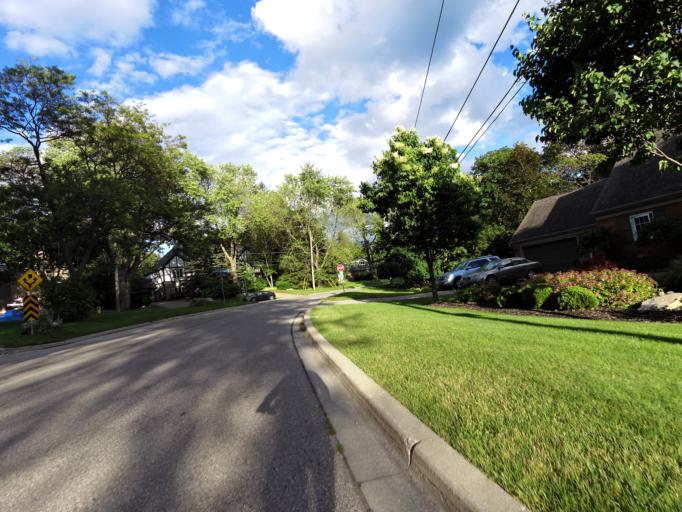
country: CA
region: Ontario
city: Scarborough
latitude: 43.7304
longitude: -79.2199
